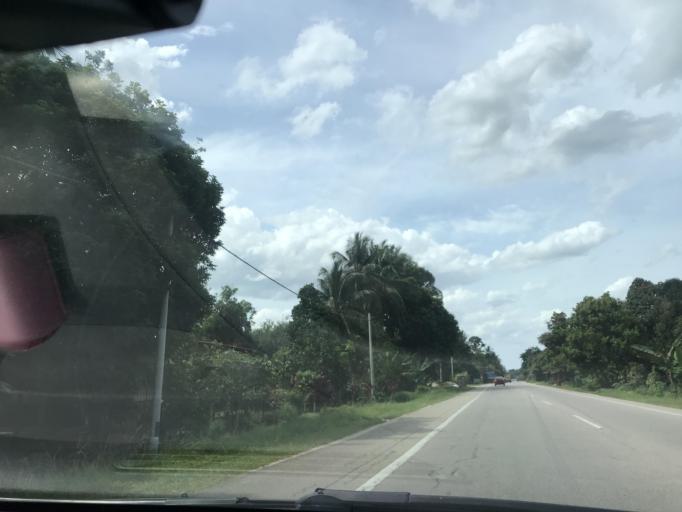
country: MY
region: Kelantan
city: Kampong Pangkal Kalong
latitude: 5.8930
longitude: 102.1826
